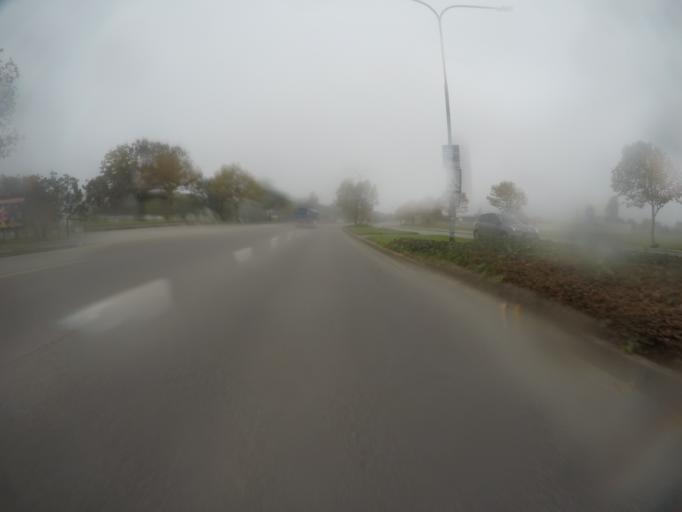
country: ZA
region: Western Cape
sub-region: Eden District Municipality
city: George
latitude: -33.9793
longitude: 22.4411
